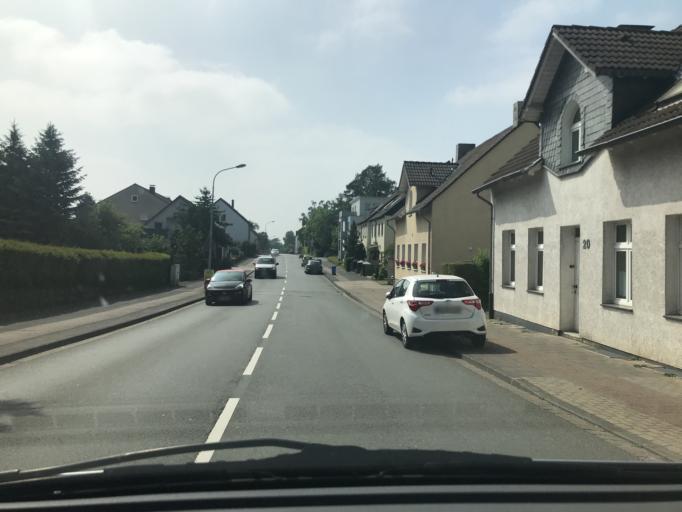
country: DE
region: North Rhine-Westphalia
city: Haan
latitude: 51.1937
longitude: 6.9941
